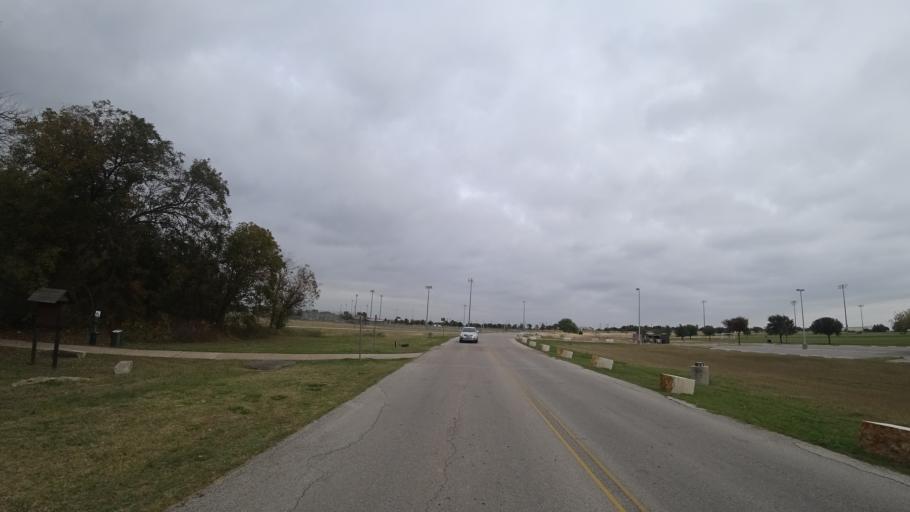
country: US
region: Texas
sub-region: Travis County
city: Pflugerville
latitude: 30.4128
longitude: -97.5993
